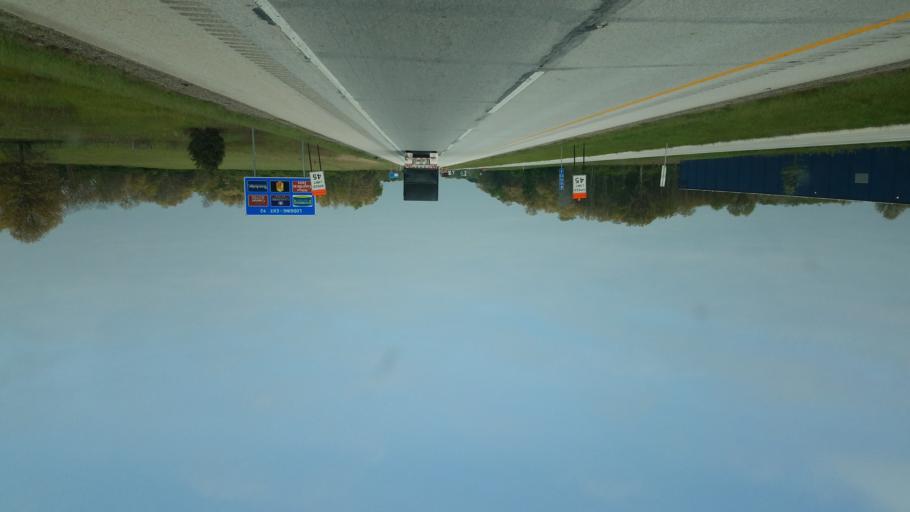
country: US
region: Indiana
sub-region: Elkhart County
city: Simonton Lake
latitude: 41.7301
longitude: -85.9312
